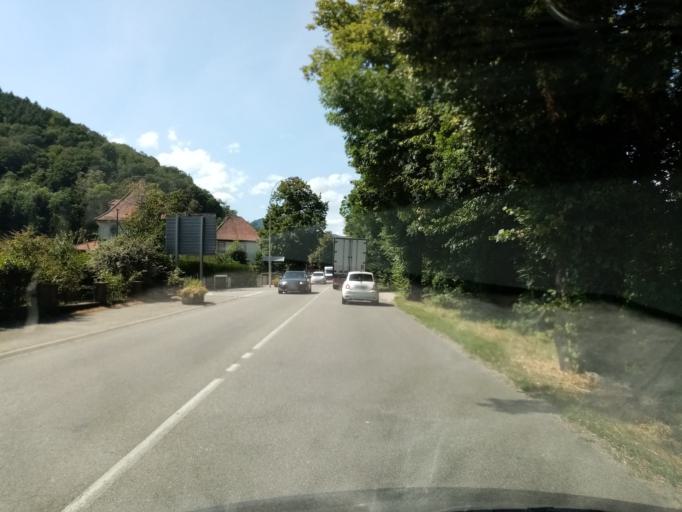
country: FR
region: Alsace
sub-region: Departement du Bas-Rhin
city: Chatenois
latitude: 48.2769
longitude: 7.3989
